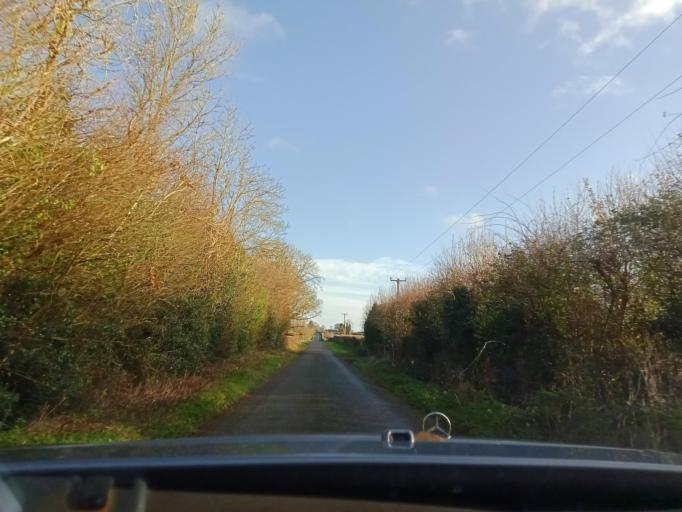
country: IE
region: Leinster
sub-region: Kilkenny
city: Callan
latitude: 52.5007
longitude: -7.4074
